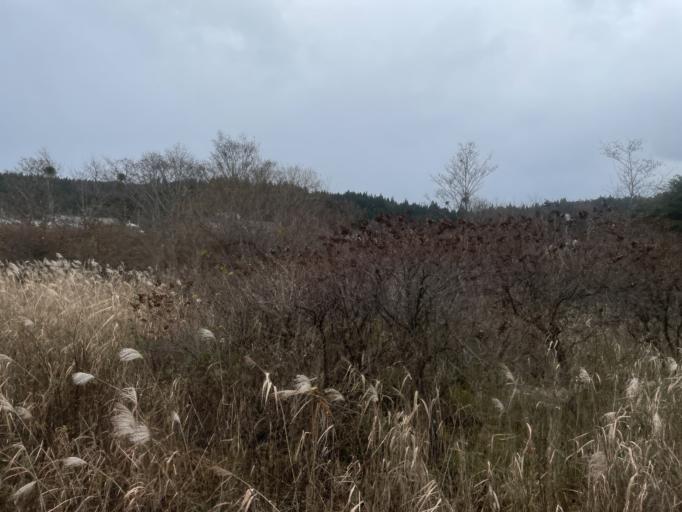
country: JP
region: Aomori
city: Goshogawara
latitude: 41.1772
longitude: 140.4935
